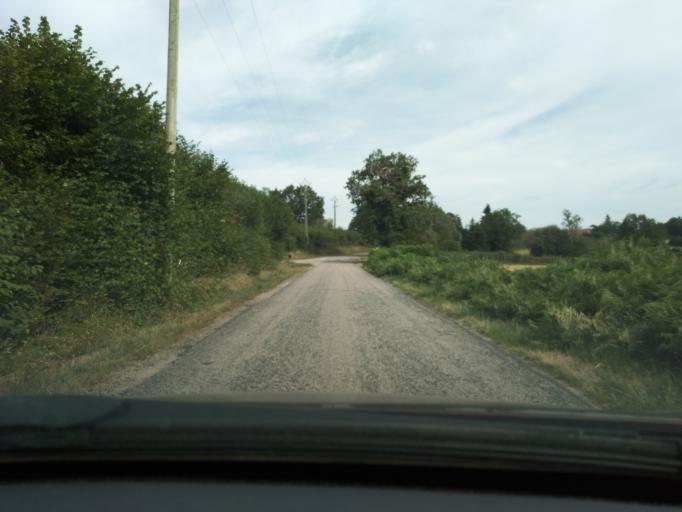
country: FR
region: Bourgogne
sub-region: Departement de la Cote-d'Or
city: Saulieu
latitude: 47.3820
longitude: 4.0764
